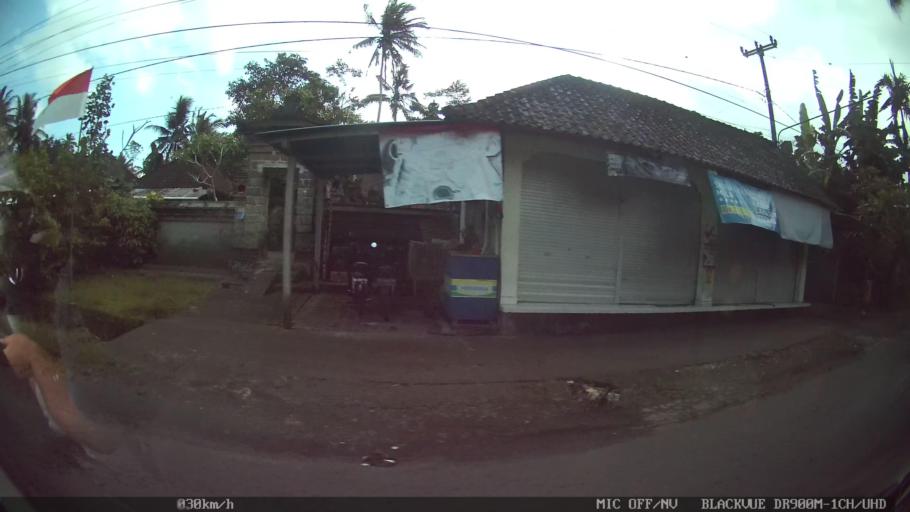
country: ID
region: Bali
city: Banjar Pesalakan
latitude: -8.4881
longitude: 115.2980
